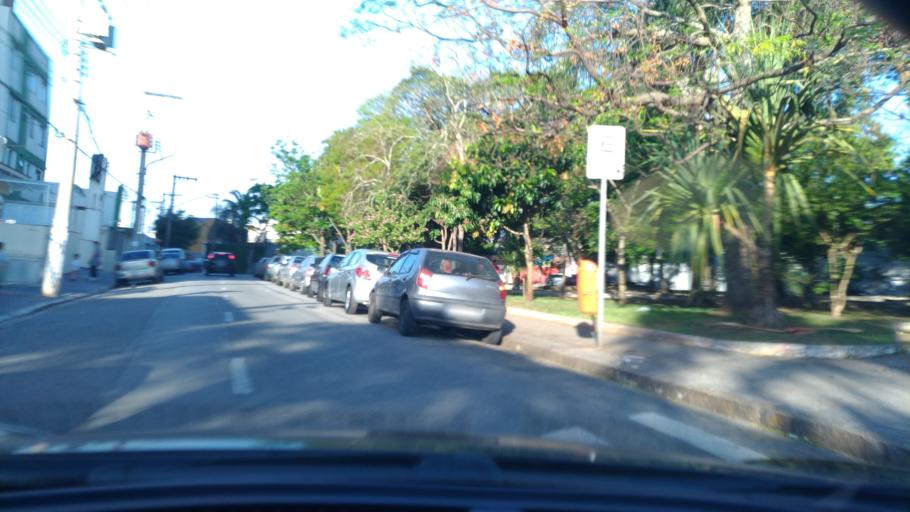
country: BR
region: Sao Paulo
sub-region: Sao Bernardo Do Campo
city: Sao Bernardo do Campo
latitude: -23.7017
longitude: -46.5557
